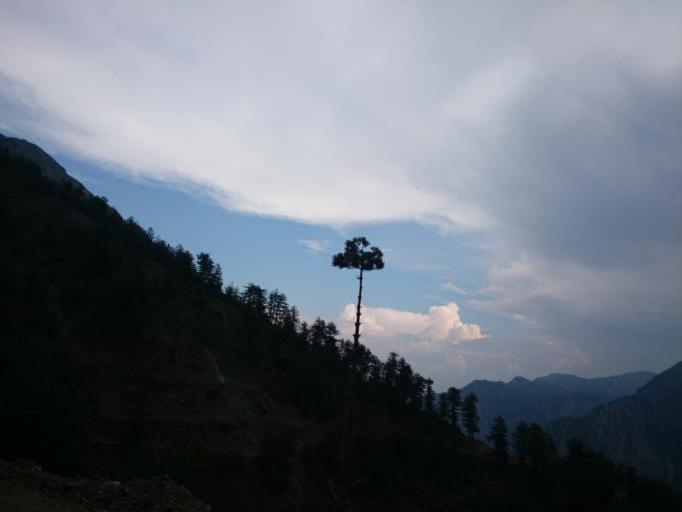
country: AL
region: Diber
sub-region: Rrethi i Dibres
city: Fushe-Lure
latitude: 41.7726
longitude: 20.2244
